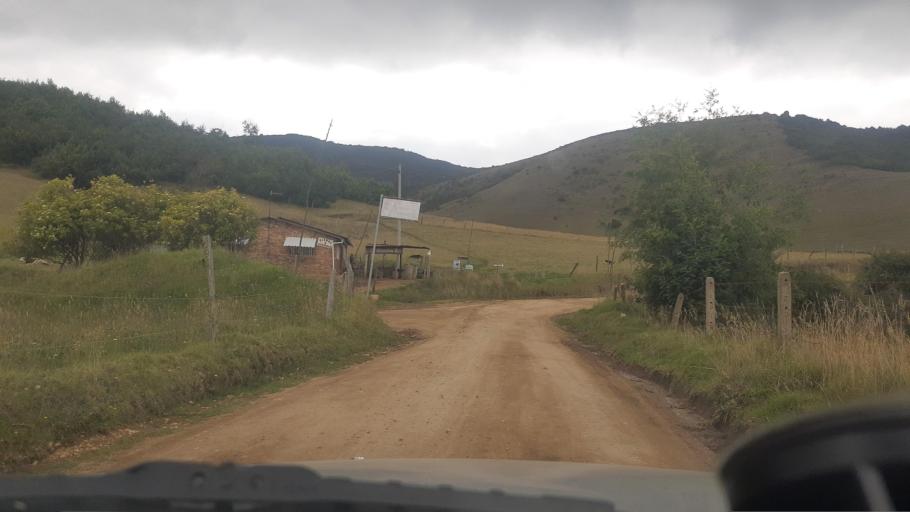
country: CO
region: Cundinamarca
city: Suesca
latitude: 5.1549
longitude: -73.7999
